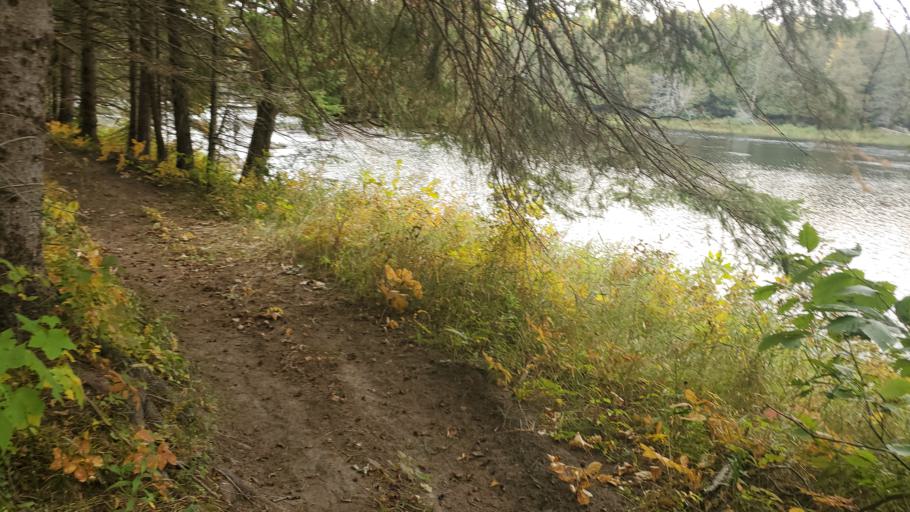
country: CA
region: Ontario
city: Renfrew
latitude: 45.2595
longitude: -77.1989
